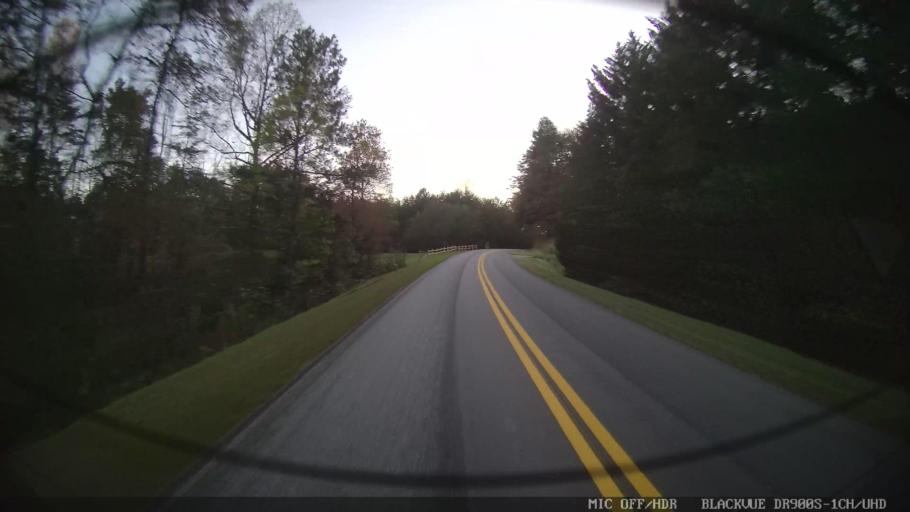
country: US
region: Georgia
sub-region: Union County
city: Blairsville
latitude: 34.8610
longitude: -83.8897
